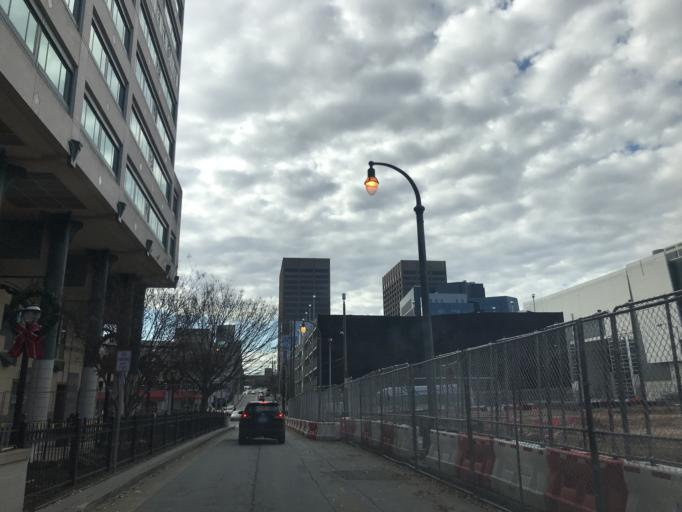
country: US
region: Georgia
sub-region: Fulton County
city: Atlanta
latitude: 33.7524
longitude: -84.3825
